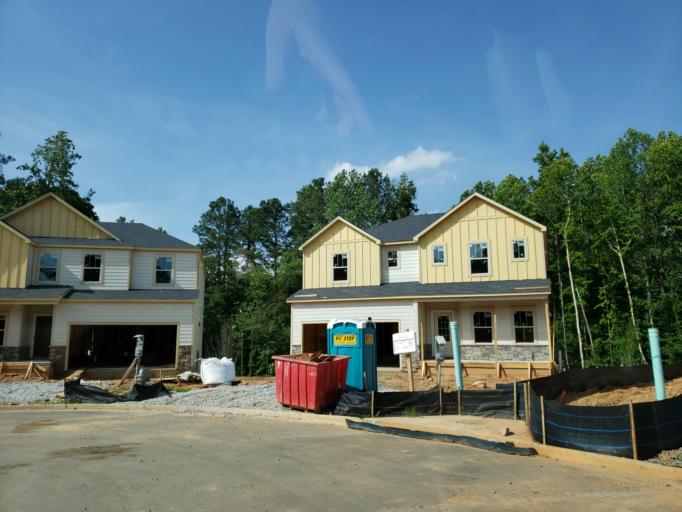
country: US
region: Georgia
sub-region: Cobb County
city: Mableton
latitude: 33.8670
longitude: -84.6122
